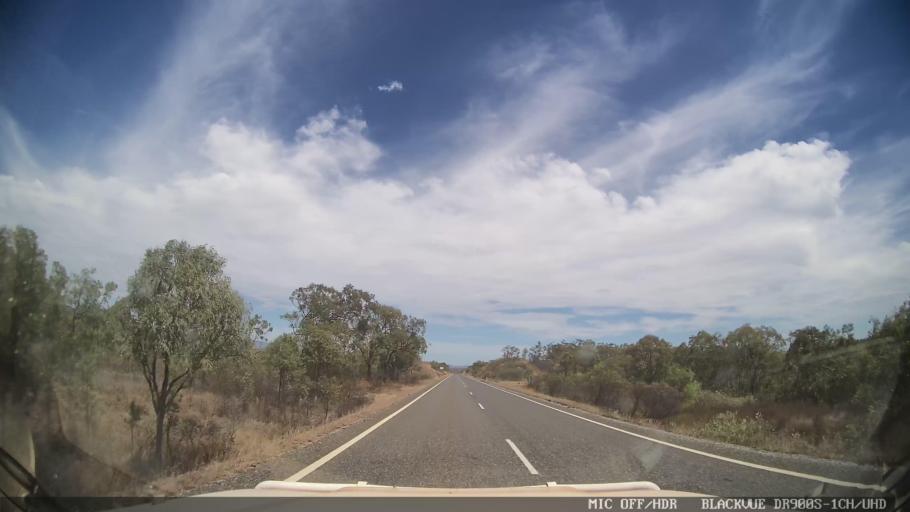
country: AU
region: Queensland
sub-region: Cook
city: Cooktown
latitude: -16.0265
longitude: 144.8101
